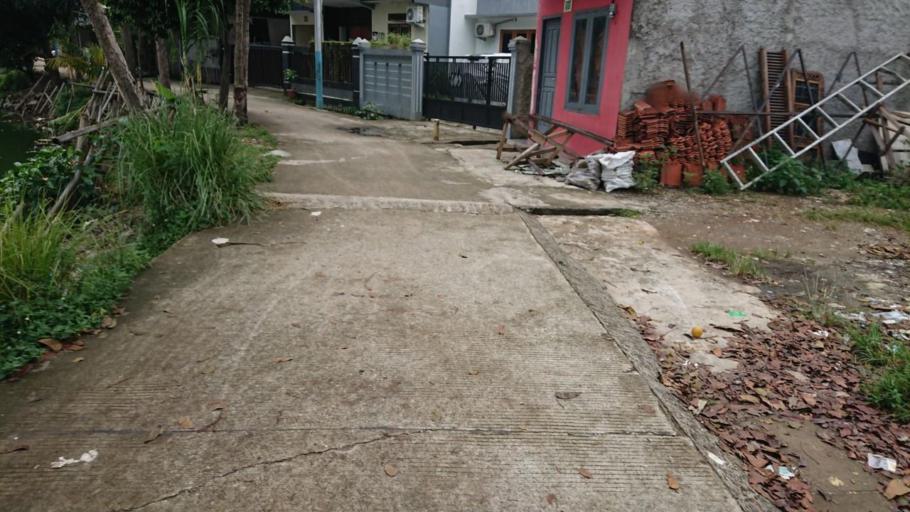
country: ID
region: West Java
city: Depok
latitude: -6.3559
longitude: 106.8688
